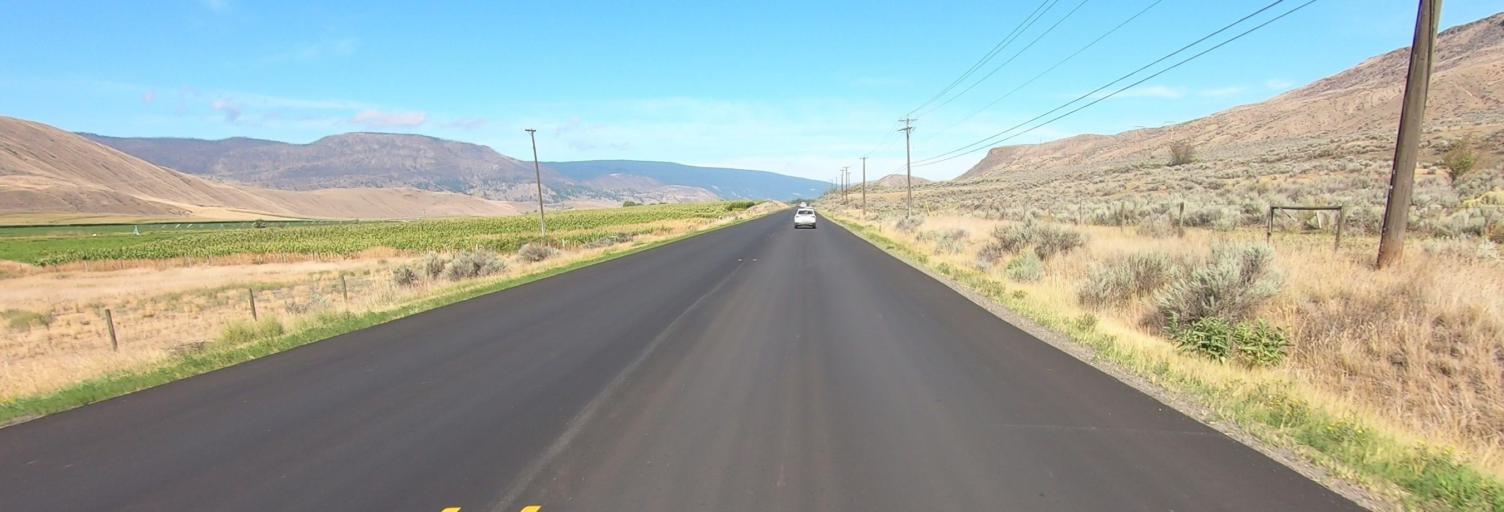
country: CA
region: British Columbia
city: Cache Creek
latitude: 50.7969
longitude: -121.2547
